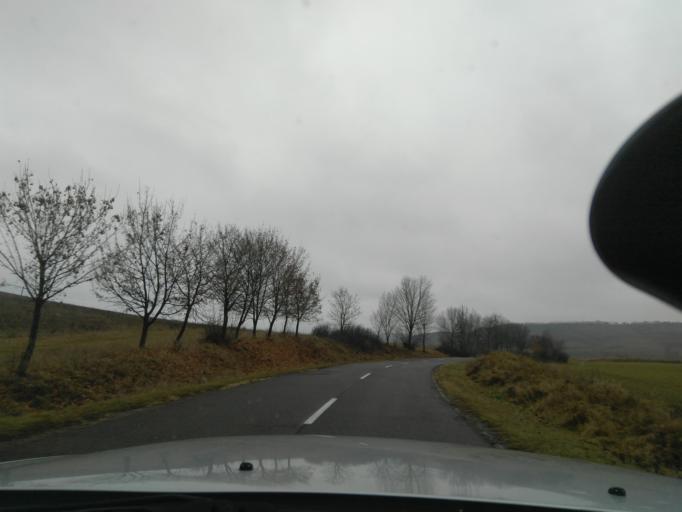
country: HU
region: Nograd
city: Kazar
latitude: 48.0340
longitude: 19.8720
